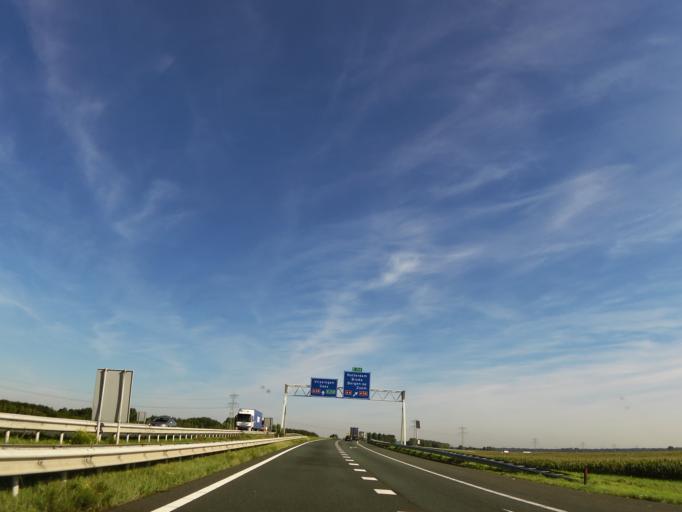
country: NL
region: North Brabant
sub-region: Gemeente Woensdrecht
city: Woensdrecht
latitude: 51.4260
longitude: 4.2762
